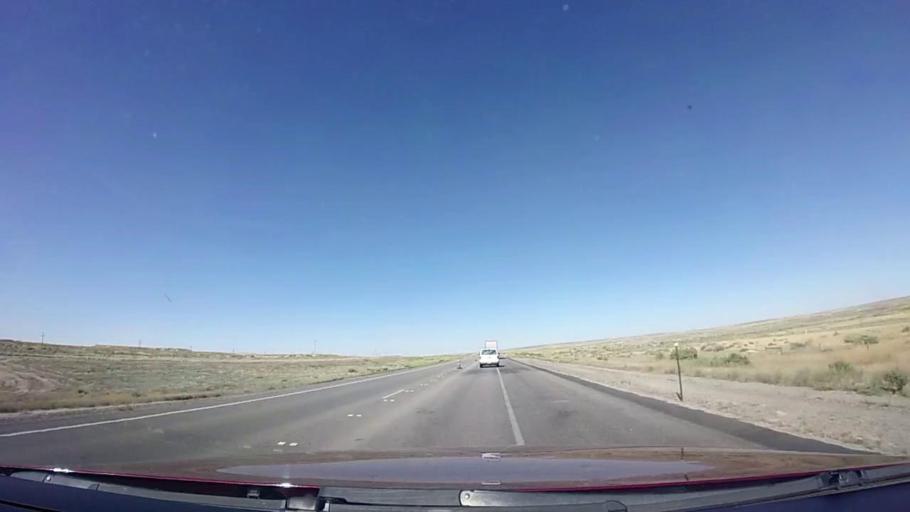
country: US
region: Wyoming
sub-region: Carbon County
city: Rawlins
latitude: 41.7058
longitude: -107.8825
